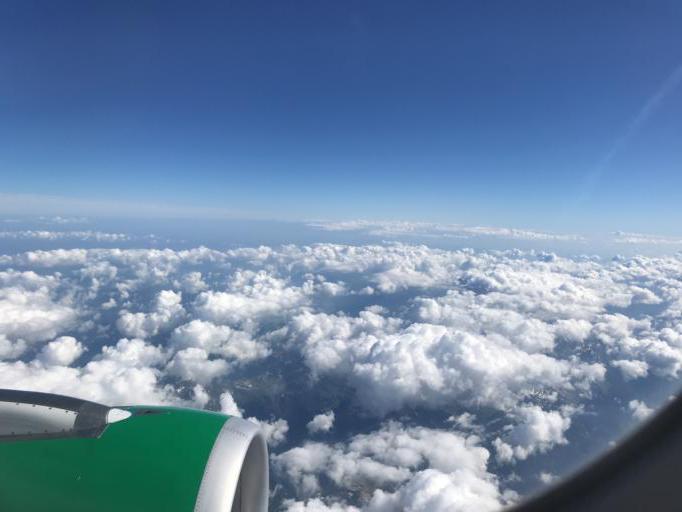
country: AT
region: Vorarlberg
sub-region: Politischer Bezirk Bludenz
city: Lech
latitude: 47.1703
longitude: 10.1618
